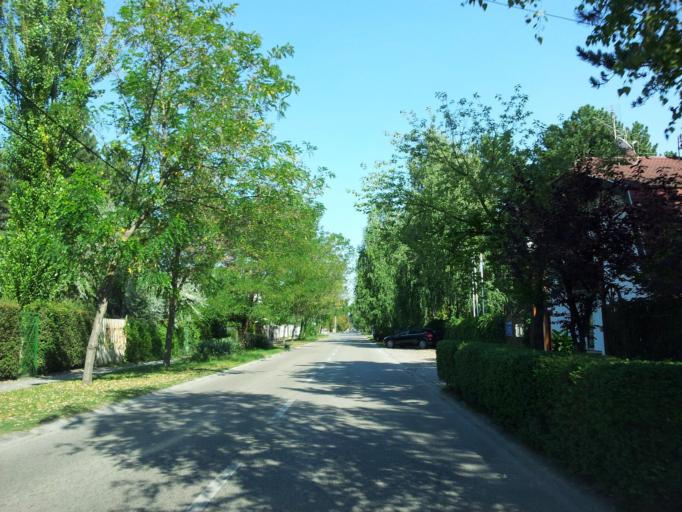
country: HU
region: Somogy
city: Zamardi
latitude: 46.8964
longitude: 18.0033
